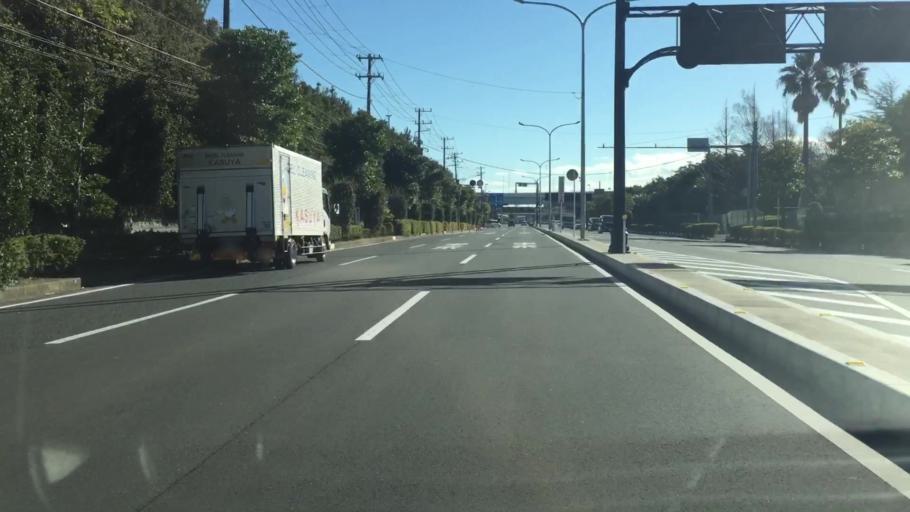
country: JP
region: Tokyo
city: Urayasu
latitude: 35.6404
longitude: 139.8807
